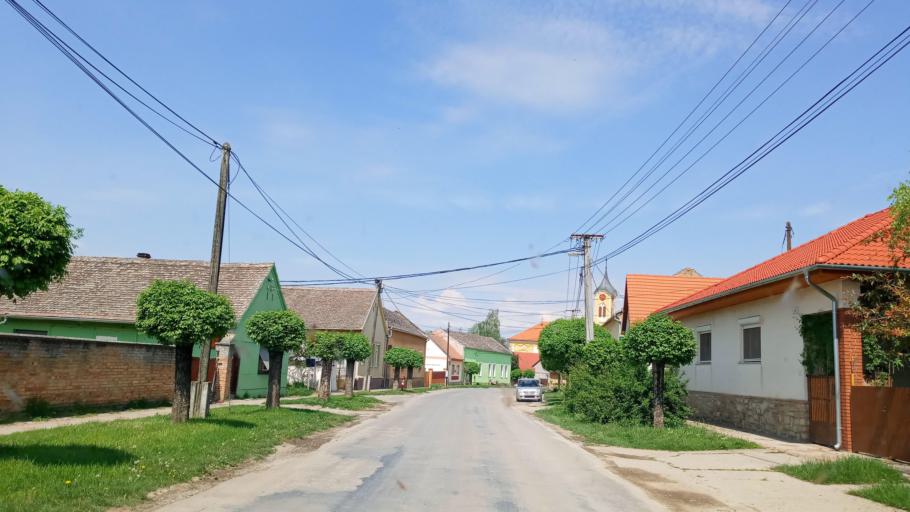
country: HU
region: Baranya
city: Boly
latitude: 45.9146
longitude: 18.5434
